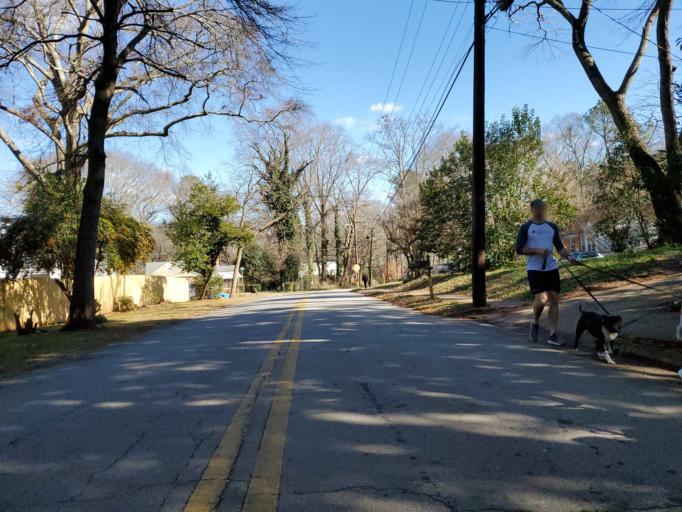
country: US
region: Georgia
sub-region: DeKalb County
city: Belvedere Park
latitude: 33.7574
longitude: -84.2801
